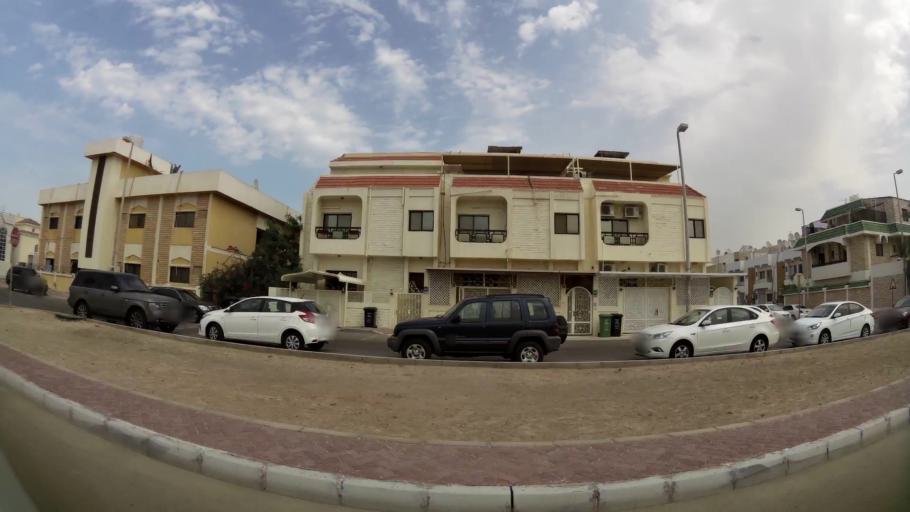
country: AE
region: Abu Dhabi
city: Abu Dhabi
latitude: 24.4637
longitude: 54.3455
